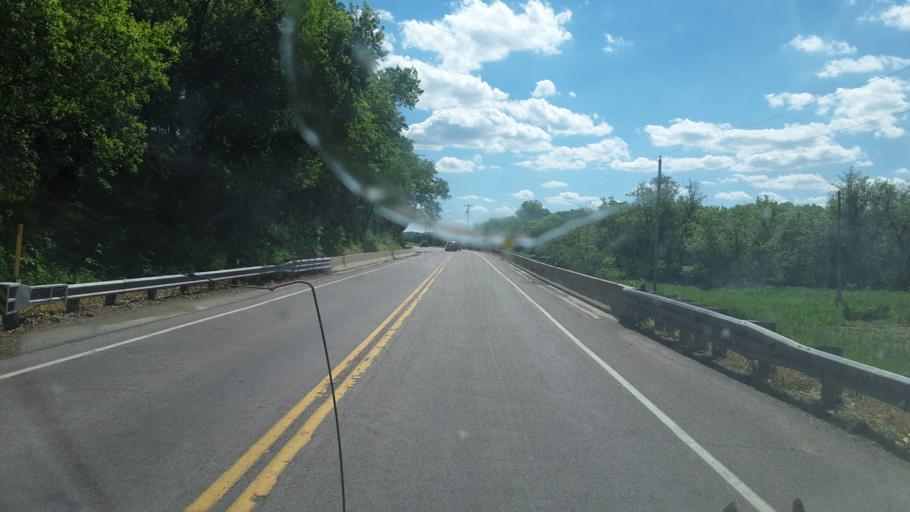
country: US
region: Wisconsin
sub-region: Richland County
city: Richland Center
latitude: 43.3545
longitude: -90.2720
